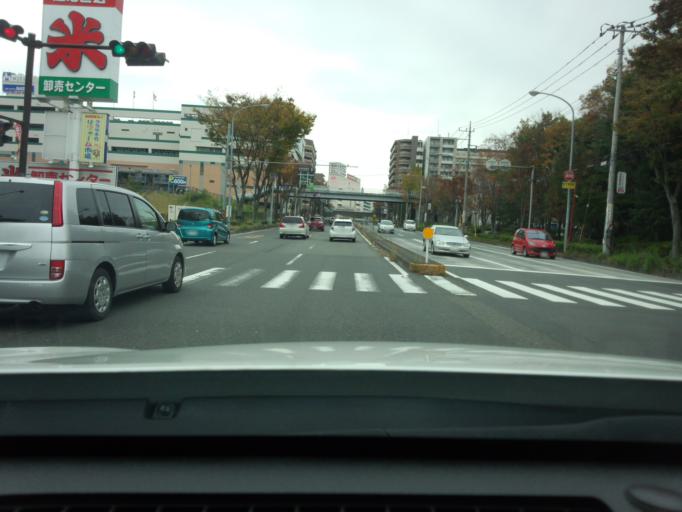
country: JP
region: Tokyo
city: Chofugaoka
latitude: 35.5488
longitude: 139.5739
